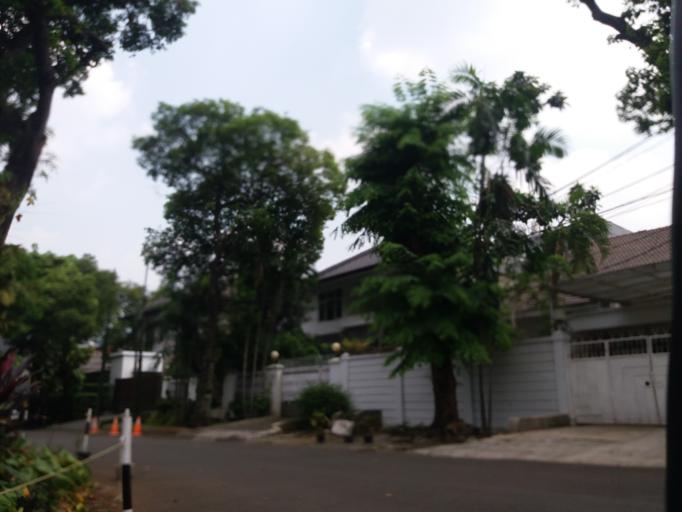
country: ID
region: Jakarta Raya
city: Jakarta
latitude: -6.2321
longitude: 106.8083
